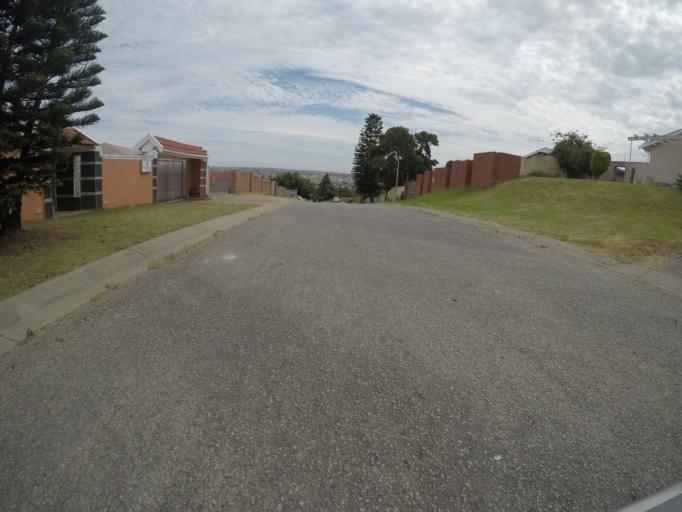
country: ZA
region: Eastern Cape
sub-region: Buffalo City Metropolitan Municipality
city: East London
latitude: -32.9978
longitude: 27.8707
